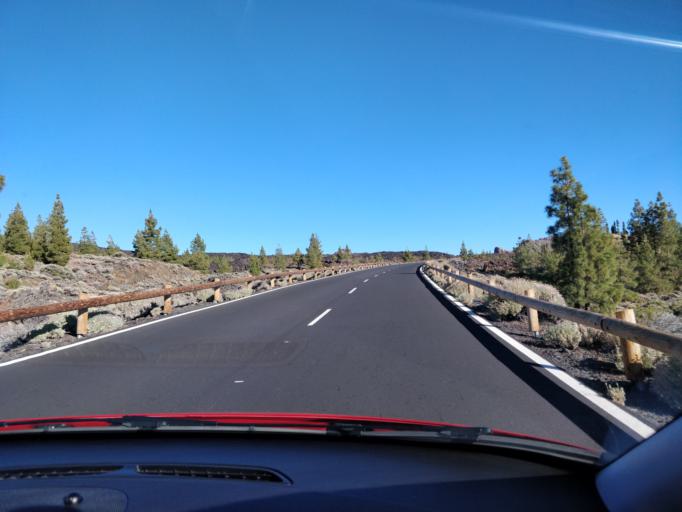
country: ES
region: Canary Islands
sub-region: Provincia de Santa Cruz de Tenerife
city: Guia de Isora
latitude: 28.2483
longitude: -16.7068
